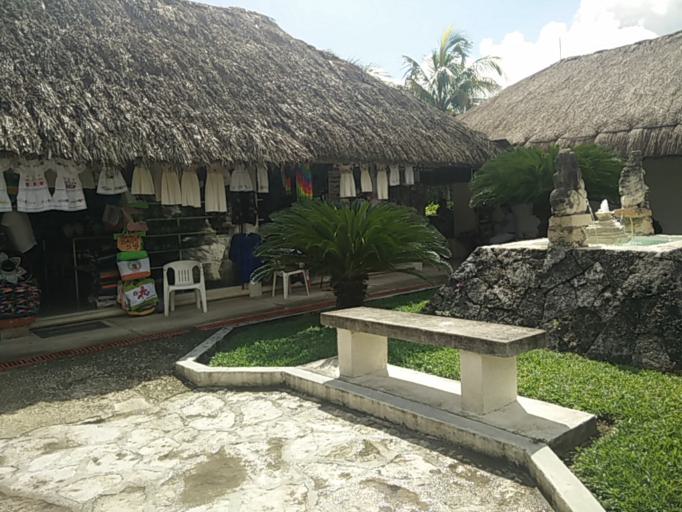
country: MX
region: Quintana Roo
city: San Miguel de Cozumel
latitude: 20.4984
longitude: -86.8451
